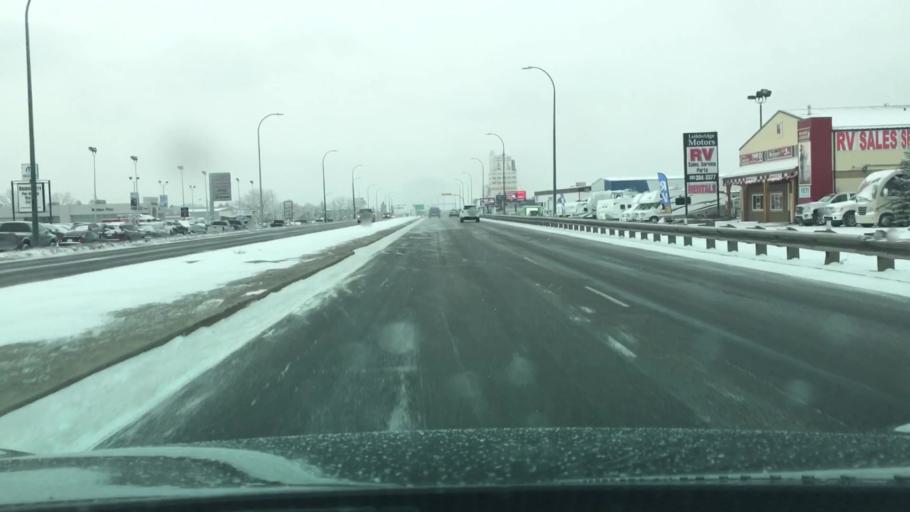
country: CA
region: Alberta
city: Lethbridge
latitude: 49.6983
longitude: -112.7906
